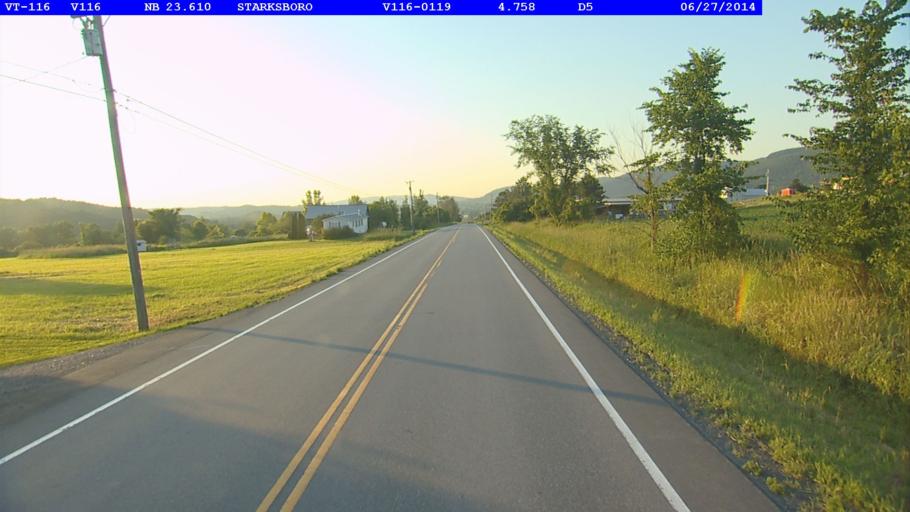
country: US
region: Vermont
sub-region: Chittenden County
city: Hinesburg
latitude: 44.2527
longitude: -73.0629
